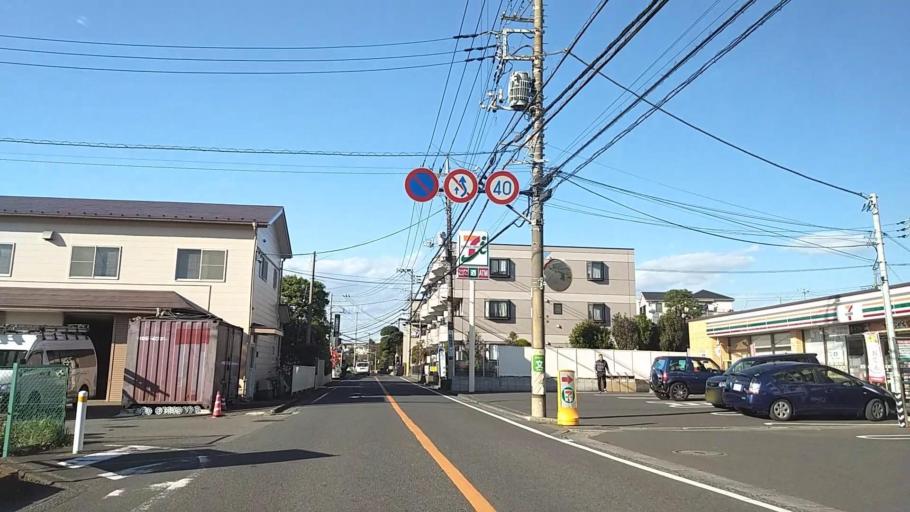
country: JP
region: Tokyo
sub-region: Machida-shi
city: Machida
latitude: 35.5403
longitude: 139.5436
